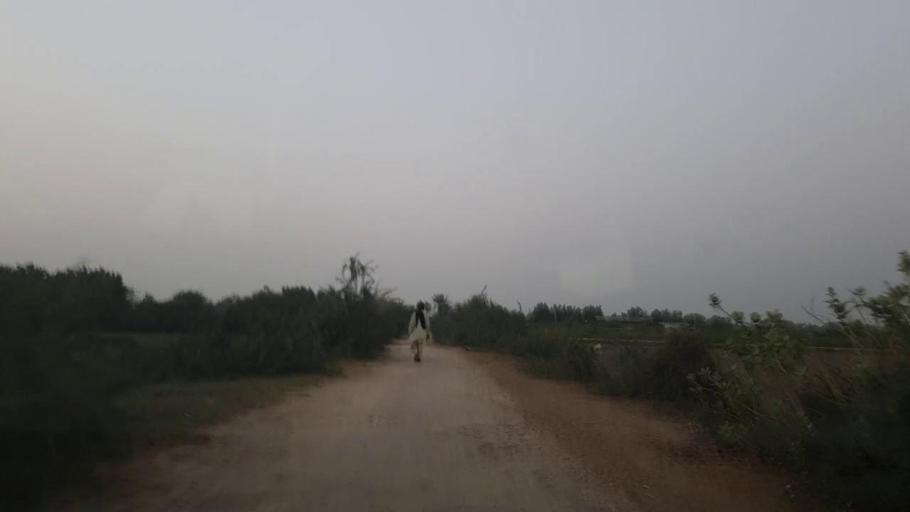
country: PK
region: Sindh
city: Mirpur Sakro
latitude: 24.5870
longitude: 67.7837
